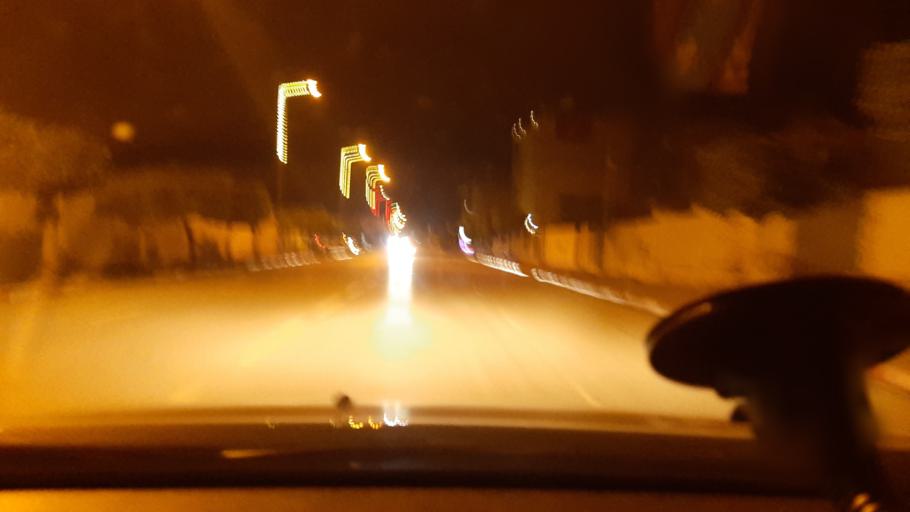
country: TN
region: Safaqis
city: Sfax
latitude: 34.7759
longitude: 10.7278
